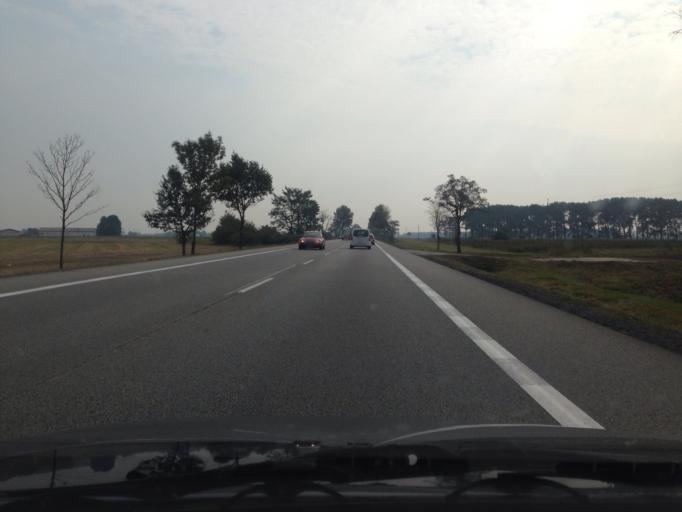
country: PL
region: Pomeranian Voivodeship
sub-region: Powiat gdanski
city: Cedry Wielkie
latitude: 54.2683
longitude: 18.8909
